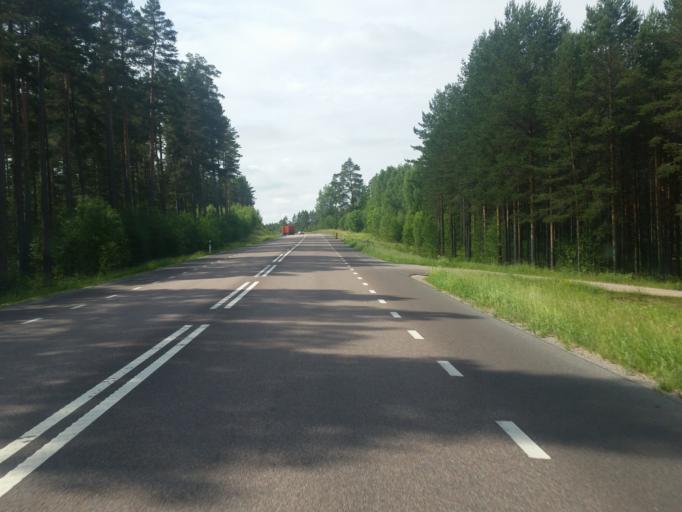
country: SE
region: Dalarna
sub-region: Gagnefs Kommun
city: Gagnef
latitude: 60.6479
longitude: 15.0640
